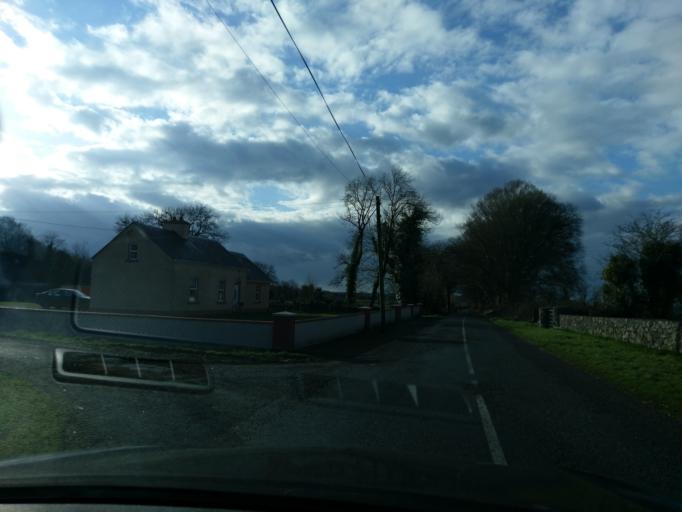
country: IE
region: Connaught
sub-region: County Galway
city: Athenry
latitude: 53.3834
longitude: -8.5866
